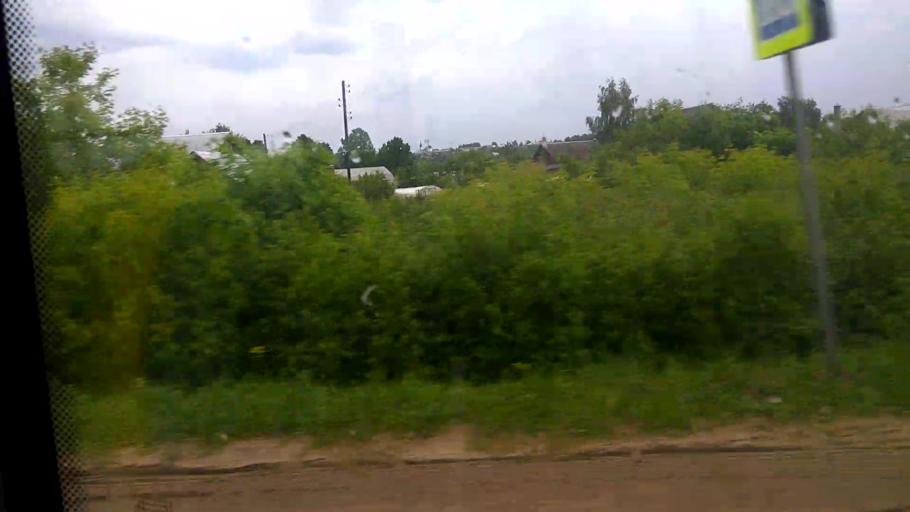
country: RU
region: Moskovskaya
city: Zaraysk
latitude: 54.7580
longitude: 38.8578
